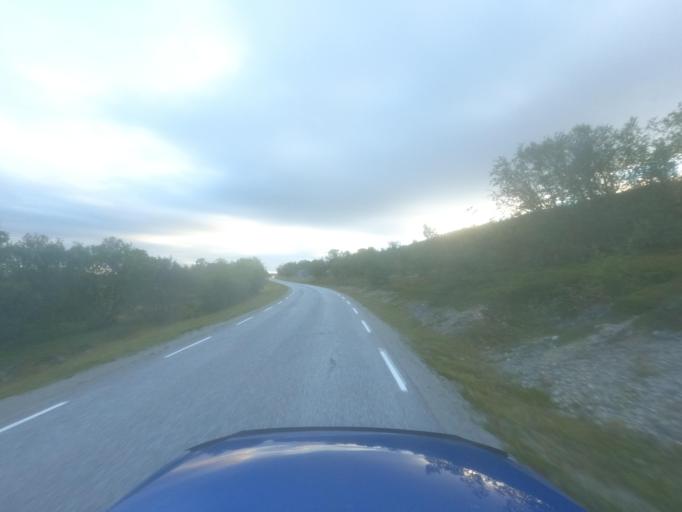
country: NO
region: Finnmark Fylke
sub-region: Porsanger
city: Lakselv
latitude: 70.3809
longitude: 25.1025
